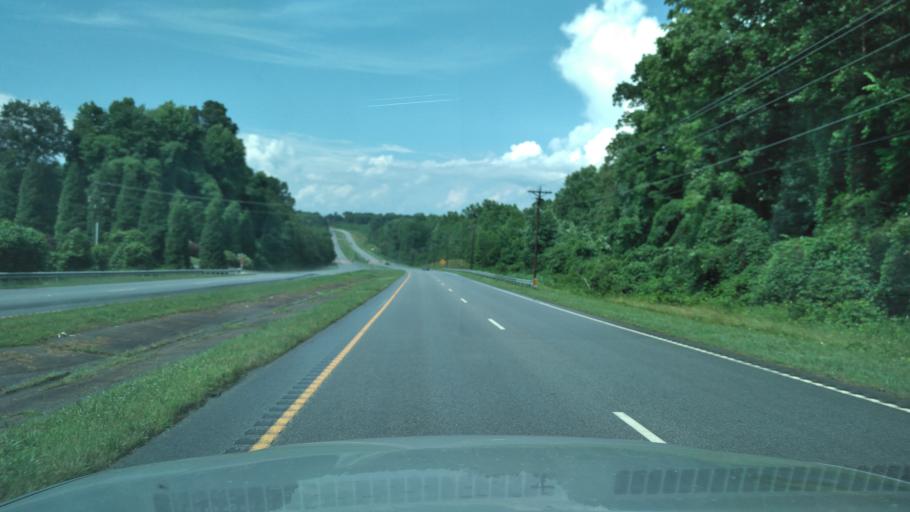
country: US
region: South Carolina
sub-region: Spartanburg County
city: Woodruff
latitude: 34.7720
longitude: -82.0288
